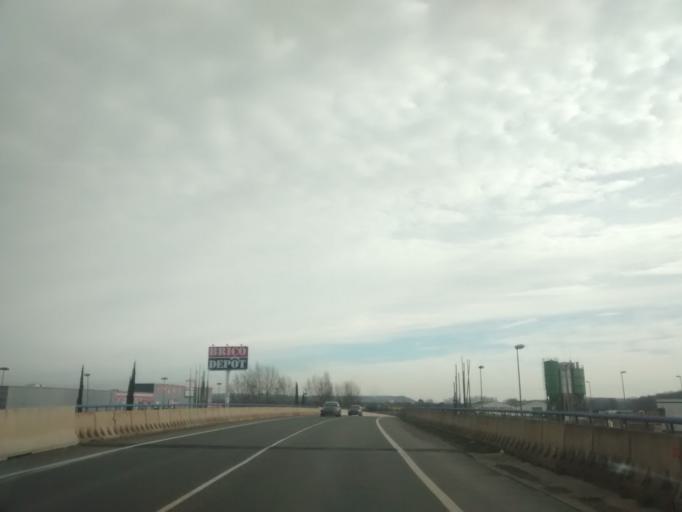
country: ES
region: Navarre
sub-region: Provincia de Navarra
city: Viana
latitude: 42.4746
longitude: -2.3970
